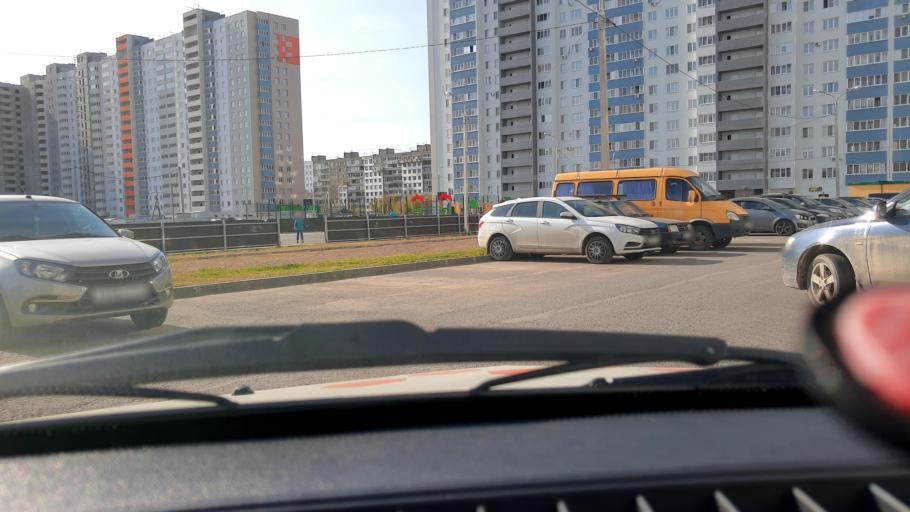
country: RU
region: Bashkortostan
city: Ufa
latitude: 54.7776
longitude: 56.1339
